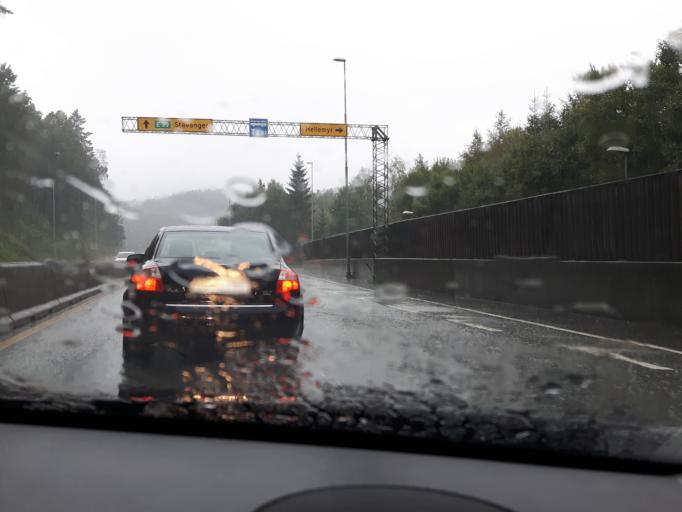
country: NO
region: Vest-Agder
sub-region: Kristiansand
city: Strai
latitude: 58.1445
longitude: 7.9227
